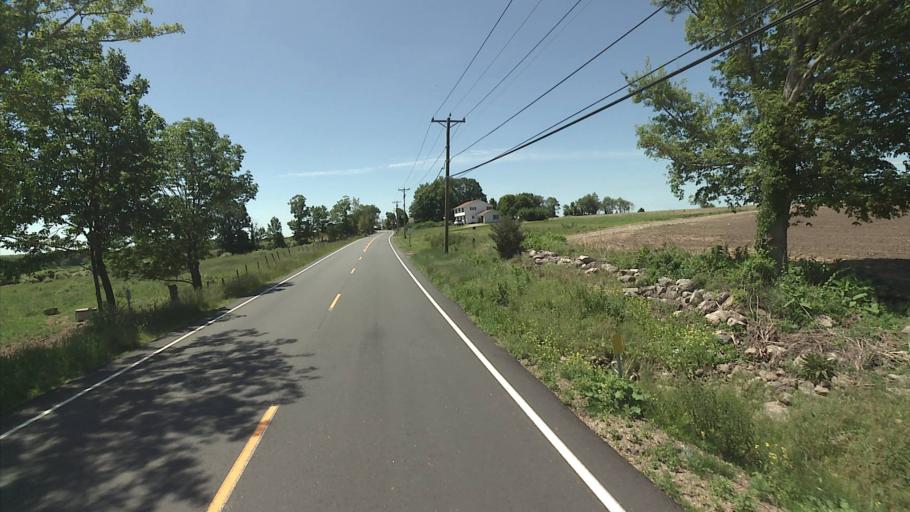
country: US
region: Connecticut
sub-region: Windham County
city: Moosup
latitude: 41.6557
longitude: -71.8479
